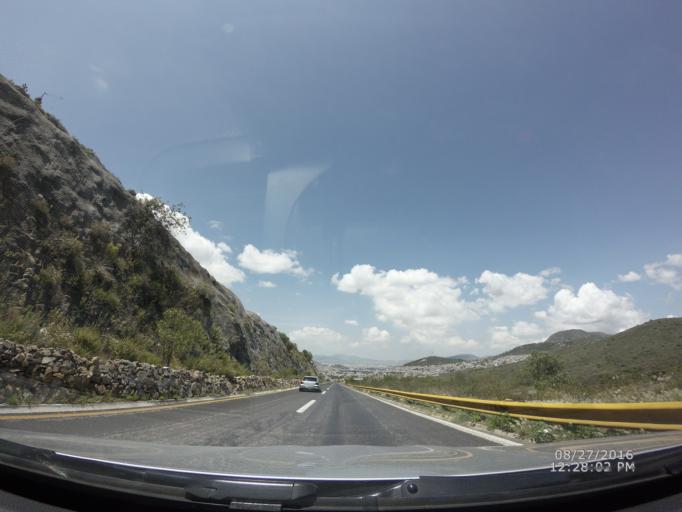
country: MX
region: Hidalgo
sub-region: Mineral de la Reforma
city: Colonia Militar
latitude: 20.1212
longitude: -98.6998
